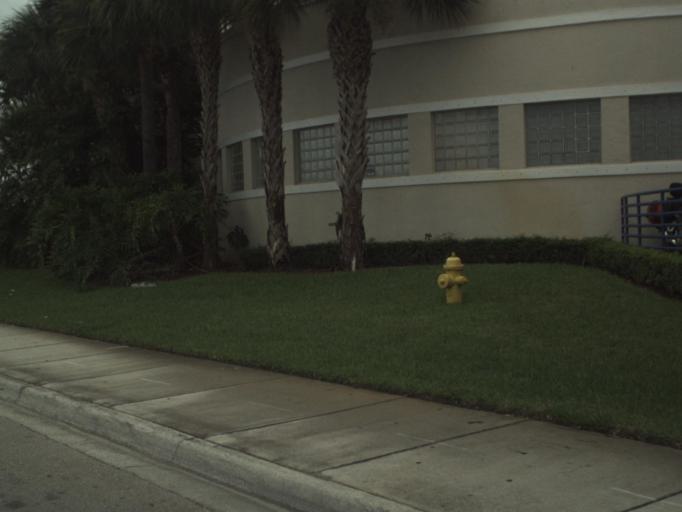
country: US
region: Florida
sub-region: Broward County
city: Pompano Beach Highlands
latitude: 26.2761
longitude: -80.1136
